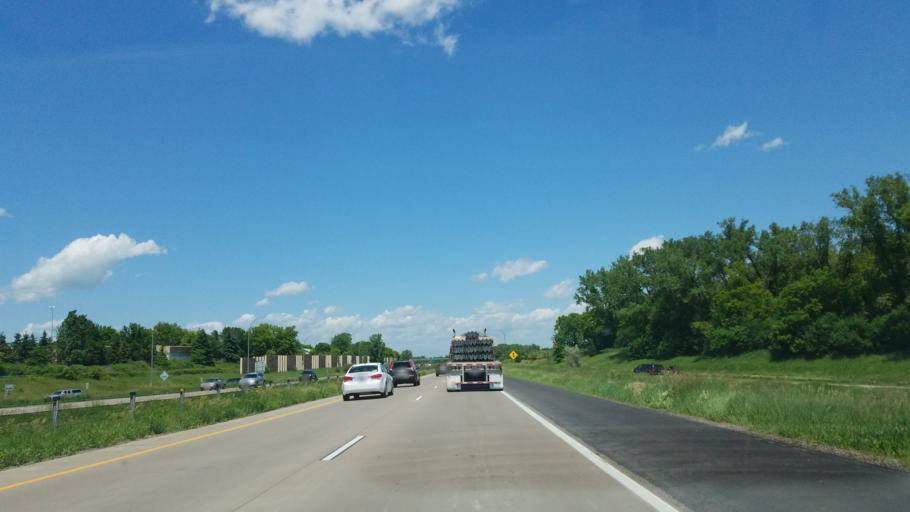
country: US
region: Minnesota
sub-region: Ramsey County
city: North Saint Paul
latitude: 44.9991
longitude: -92.9588
